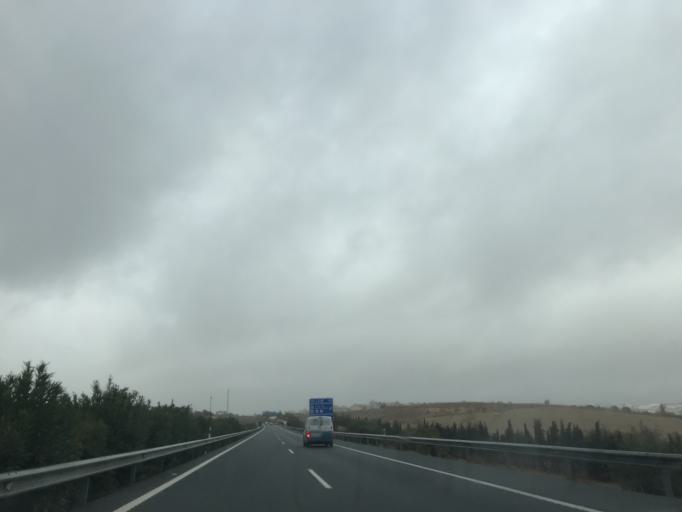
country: ES
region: Andalusia
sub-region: Provincia de Malaga
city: Mollina
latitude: 37.1093
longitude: -4.6566
